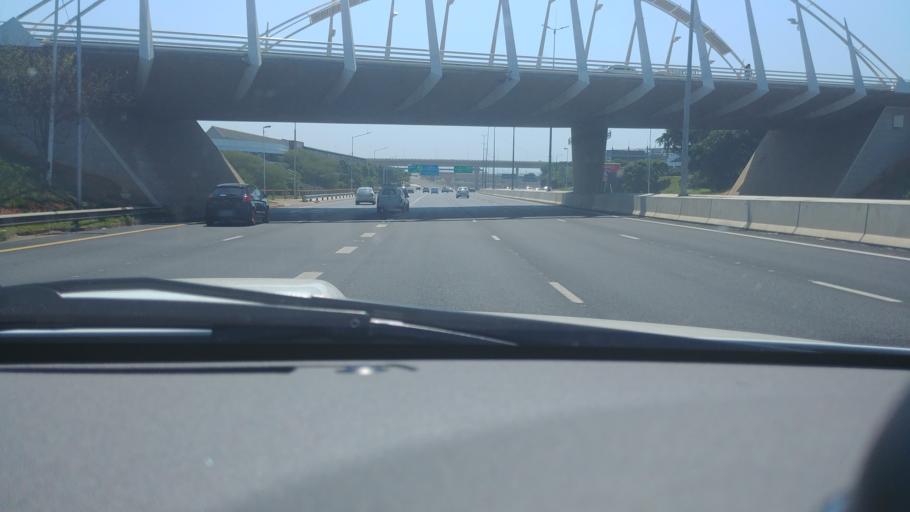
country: ZA
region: KwaZulu-Natal
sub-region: eThekwini Metropolitan Municipality
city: Durban
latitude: -29.7282
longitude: 31.0631
